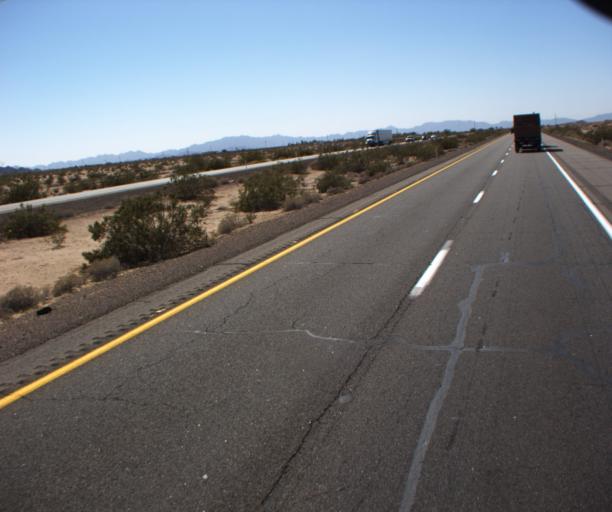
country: US
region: Arizona
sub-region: Yuma County
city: Wellton
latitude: 32.6898
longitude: -113.9787
